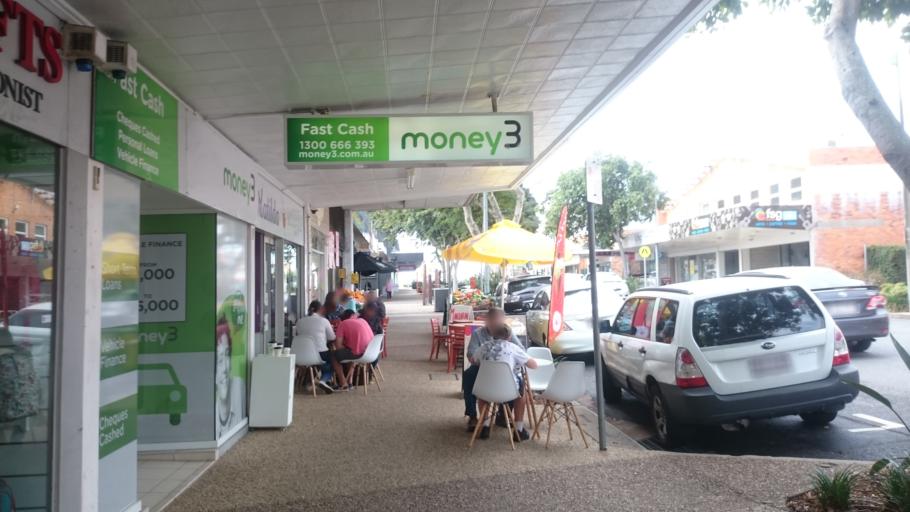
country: AU
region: Queensland
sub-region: Brisbane
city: Wynnum
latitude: -27.4450
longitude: 153.1734
